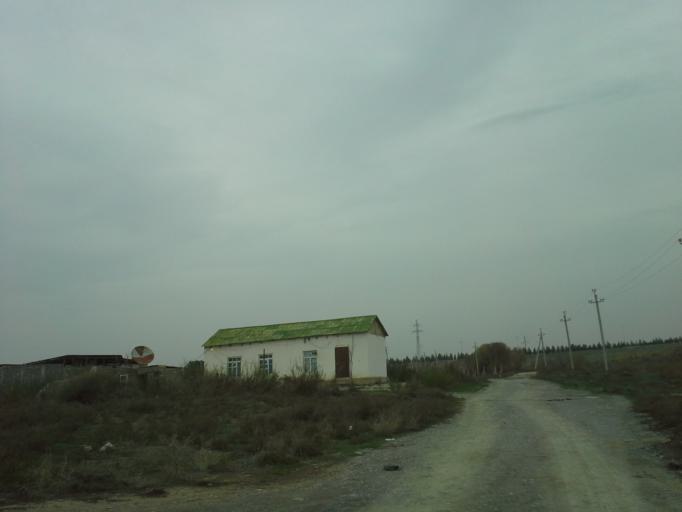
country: TM
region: Ahal
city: Abadan
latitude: 37.9791
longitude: 58.2264
